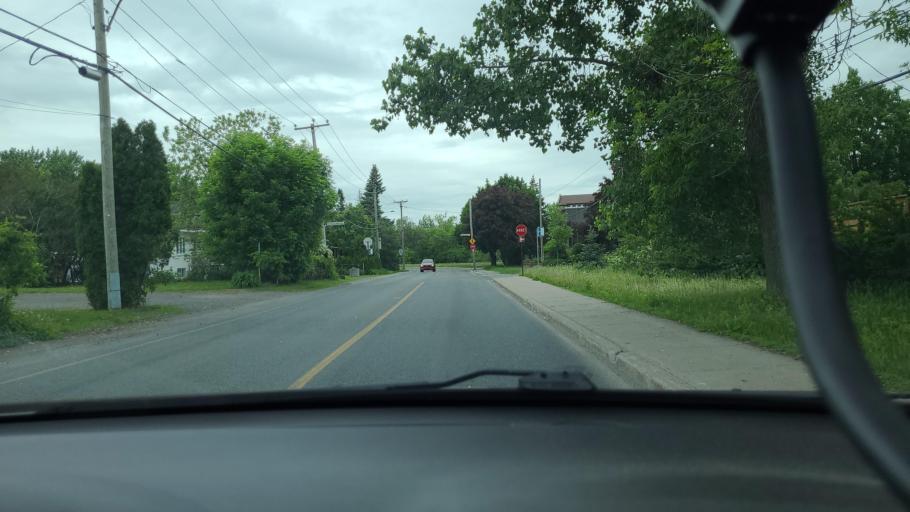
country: CA
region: Quebec
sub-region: Lanaudiere
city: Charlemagne
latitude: 45.6975
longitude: -73.4937
